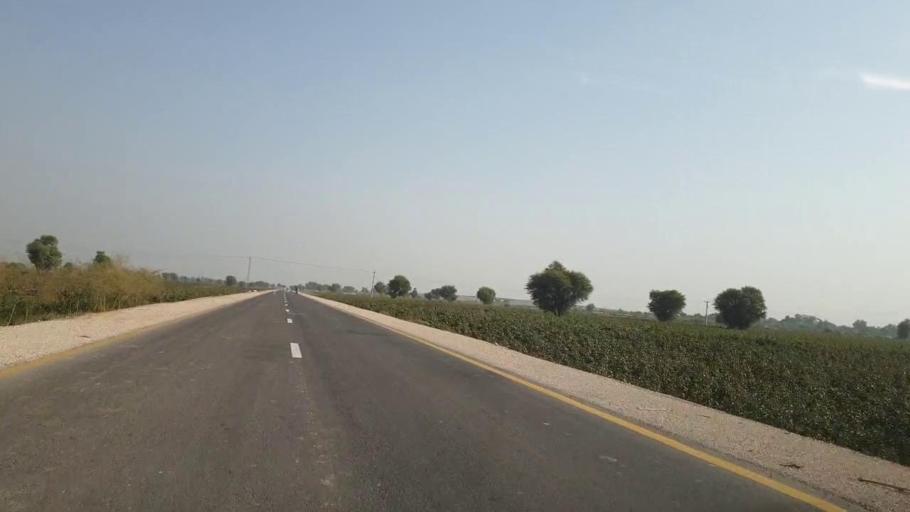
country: PK
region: Sindh
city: Sehwan
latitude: 26.4647
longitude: 67.7985
